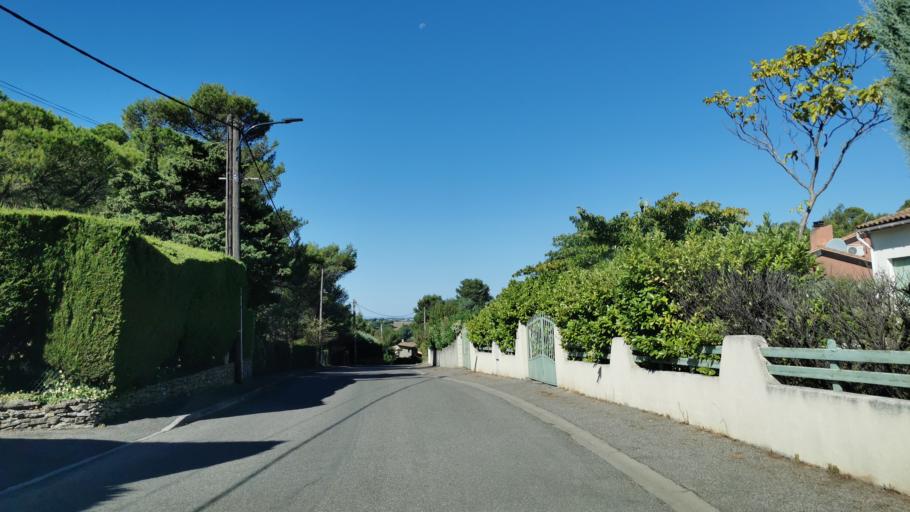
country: FR
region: Languedoc-Roussillon
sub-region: Departement de l'Aude
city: Conques-sur-Orbiel
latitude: 43.2510
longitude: 2.4472
